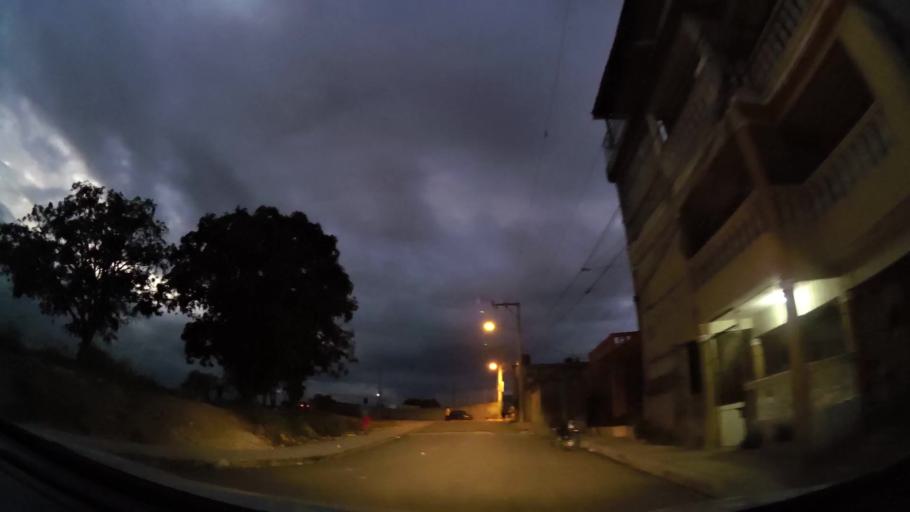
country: DO
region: Santo Domingo
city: Santo Domingo Oeste
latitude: 18.5190
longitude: -70.0167
